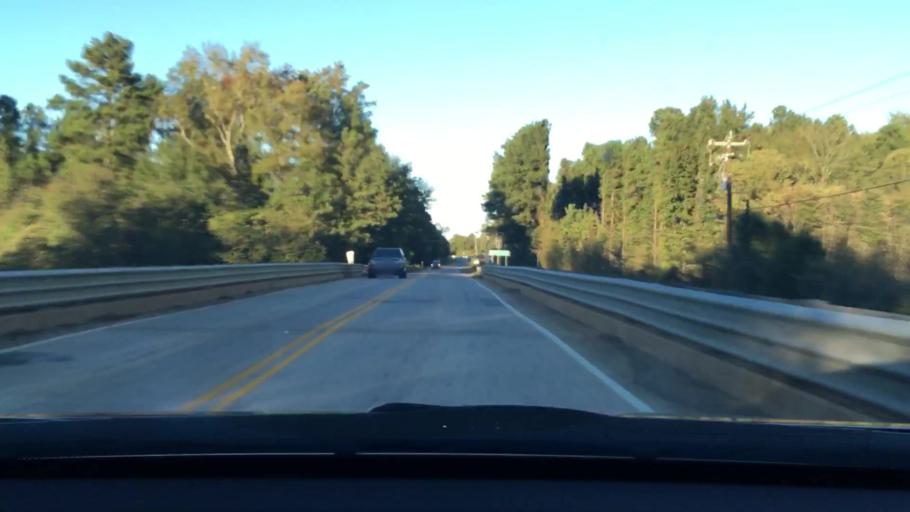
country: US
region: South Carolina
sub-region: Lexington County
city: Irmo
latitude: 34.1223
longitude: -81.1992
